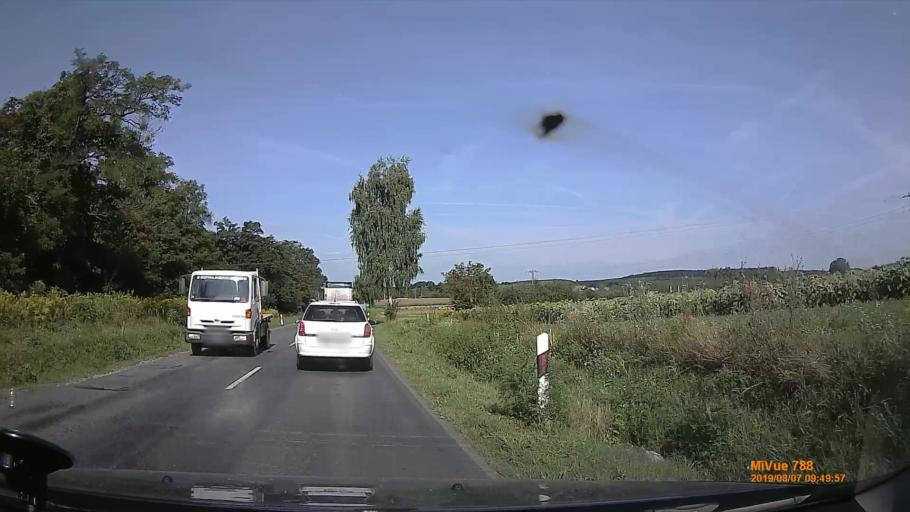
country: HU
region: Zala
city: Pacsa
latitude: 46.7419
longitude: 16.9277
